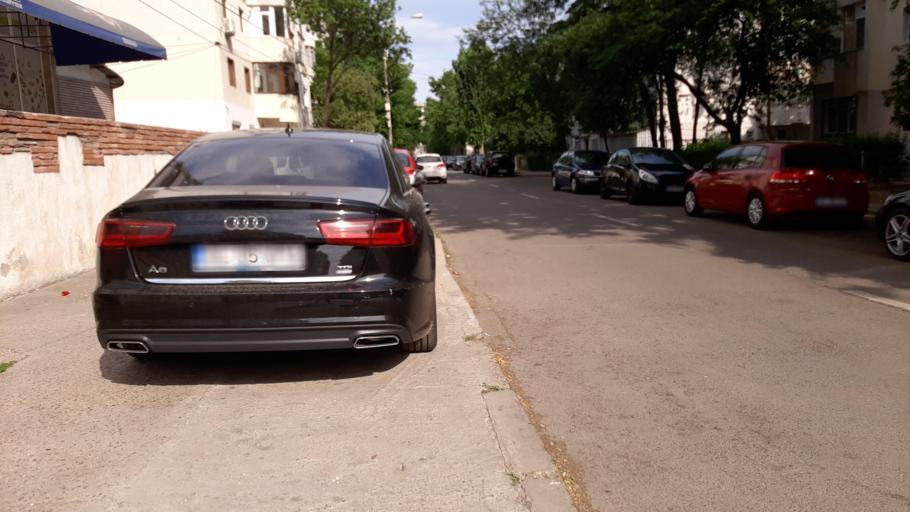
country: RO
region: Galati
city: Galati
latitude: 45.4435
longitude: 28.0248
